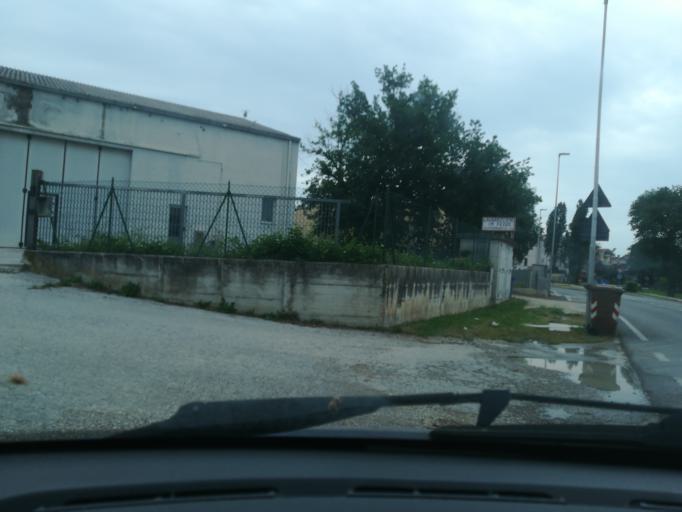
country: IT
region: The Marches
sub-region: Provincia di Macerata
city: Passo di Treia
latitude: 43.2793
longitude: 13.3226
